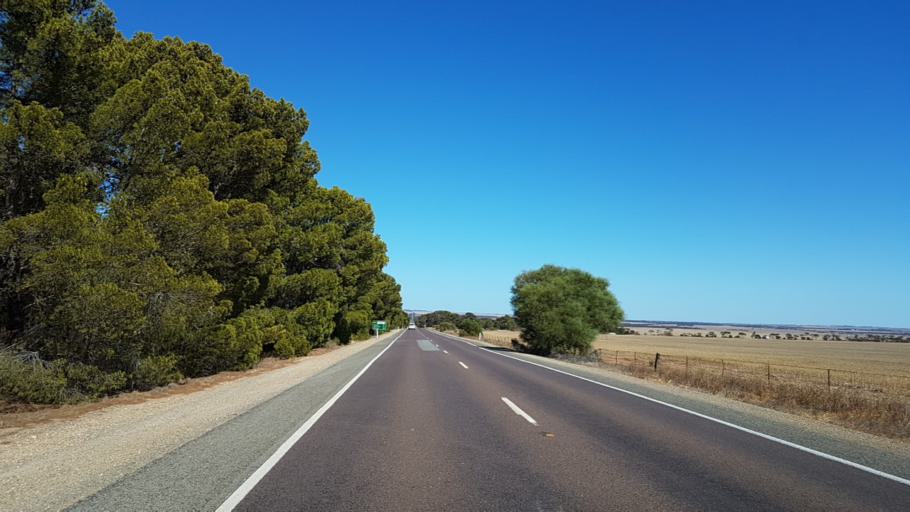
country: AU
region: South Australia
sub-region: Copper Coast
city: Kadina
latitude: -34.0590
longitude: 138.0328
